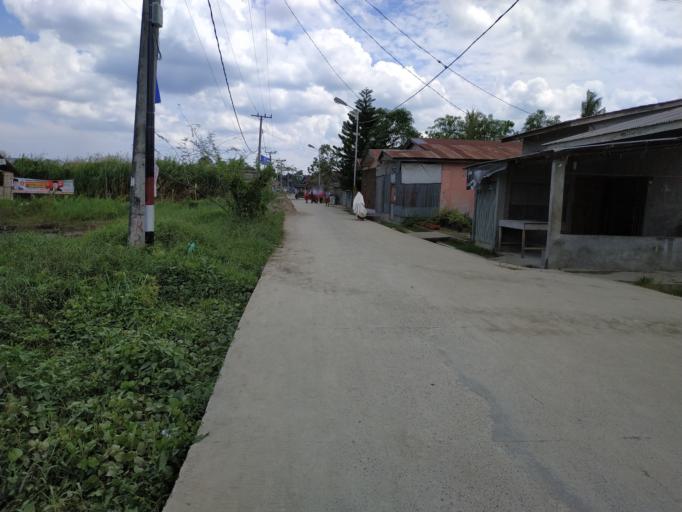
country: ID
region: North Sumatra
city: Tanjungbalai
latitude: 2.9595
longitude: 99.8144
